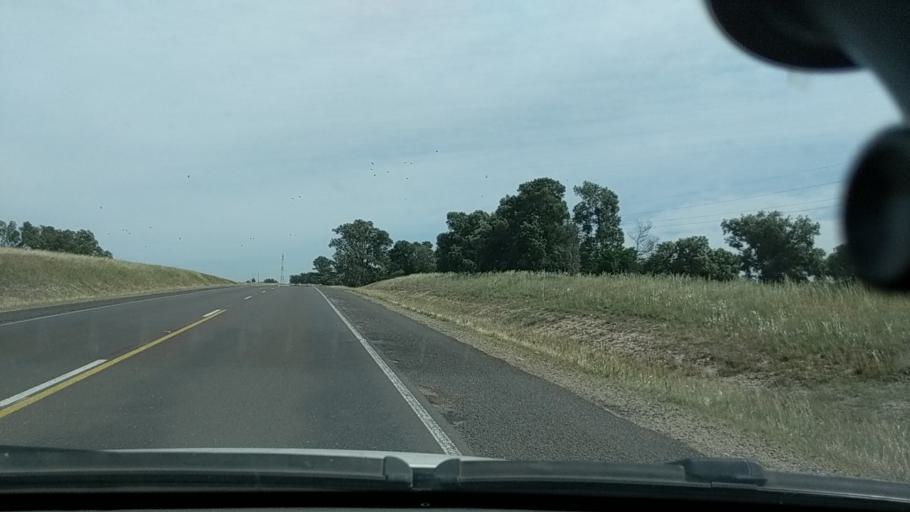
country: UY
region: Durazno
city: Durazno
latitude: -33.5084
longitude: -56.4164
